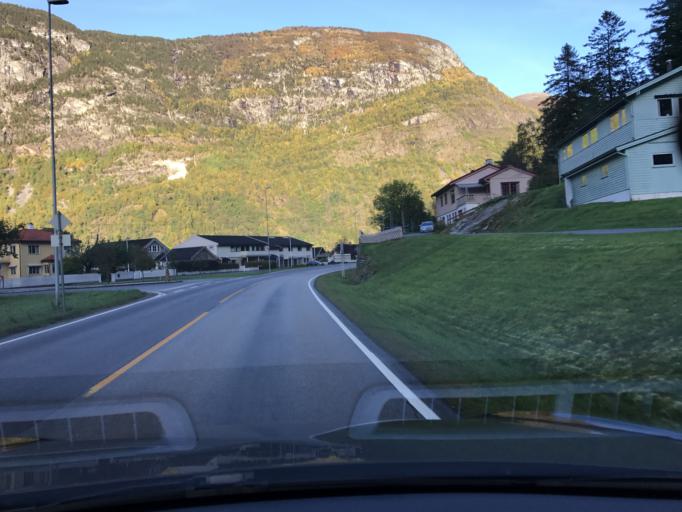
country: NO
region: Sogn og Fjordane
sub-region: Laerdal
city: Laerdalsoyri
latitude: 61.0999
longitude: 7.4996
